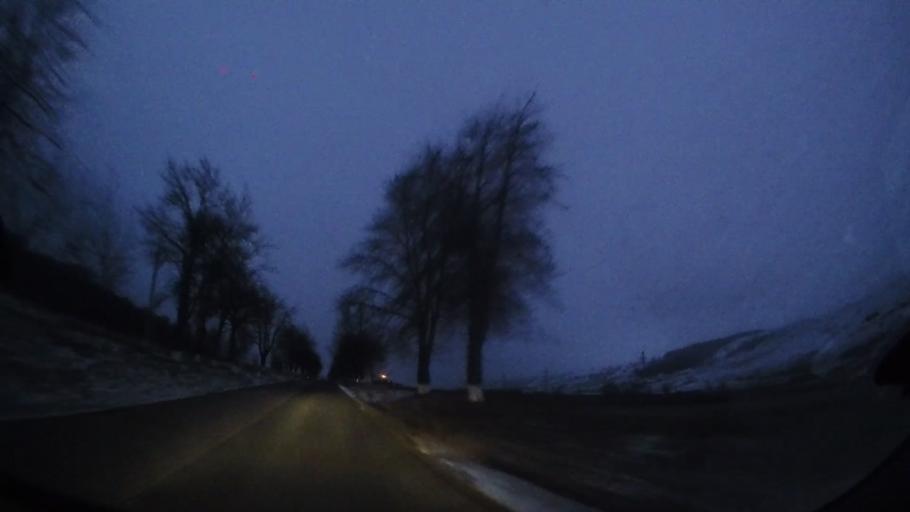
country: RO
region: Vaslui
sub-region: Comuna Hoceni
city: Hoceni
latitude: 46.5593
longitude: 27.9979
